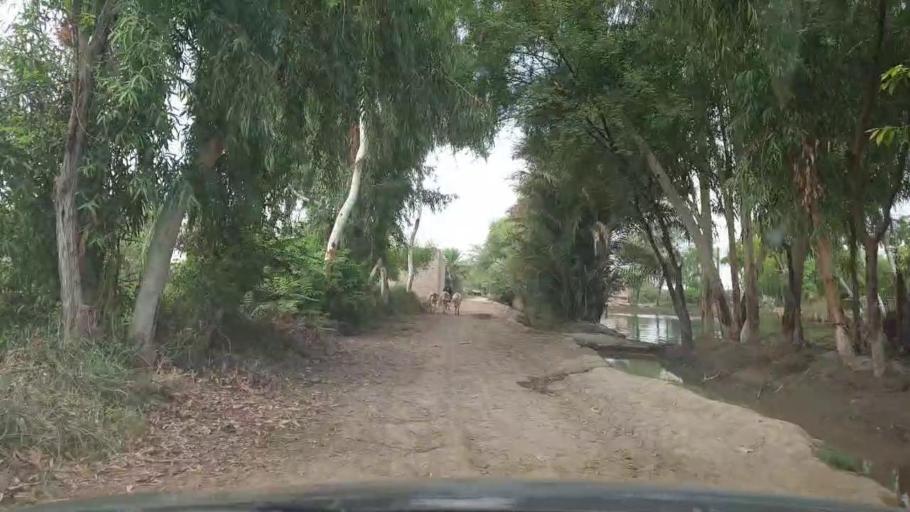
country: PK
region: Sindh
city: Ratodero
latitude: 27.8580
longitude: 68.2916
